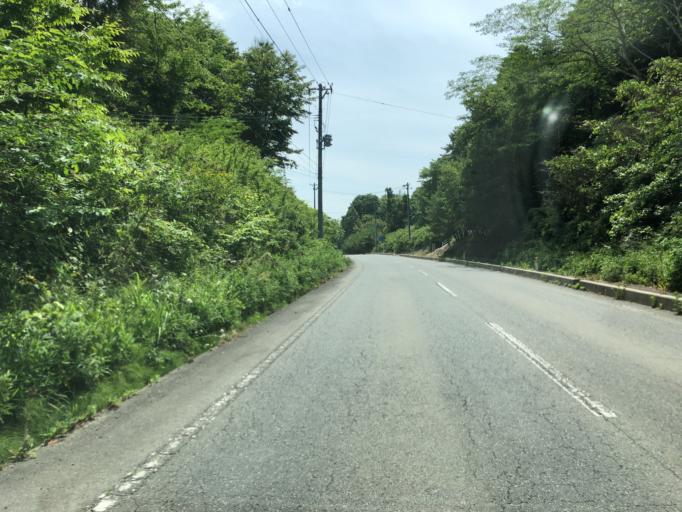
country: JP
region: Fukushima
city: Namie
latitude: 37.5728
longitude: 140.9343
